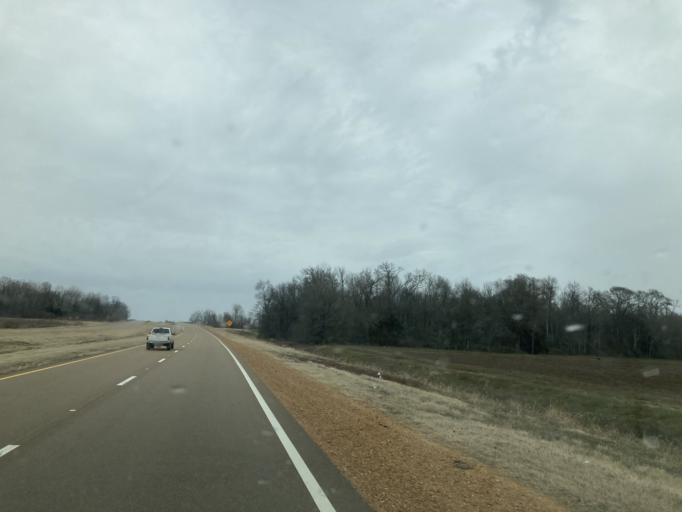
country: US
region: Mississippi
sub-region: Humphreys County
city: Belzoni
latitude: 33.0489
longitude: -90.4672
